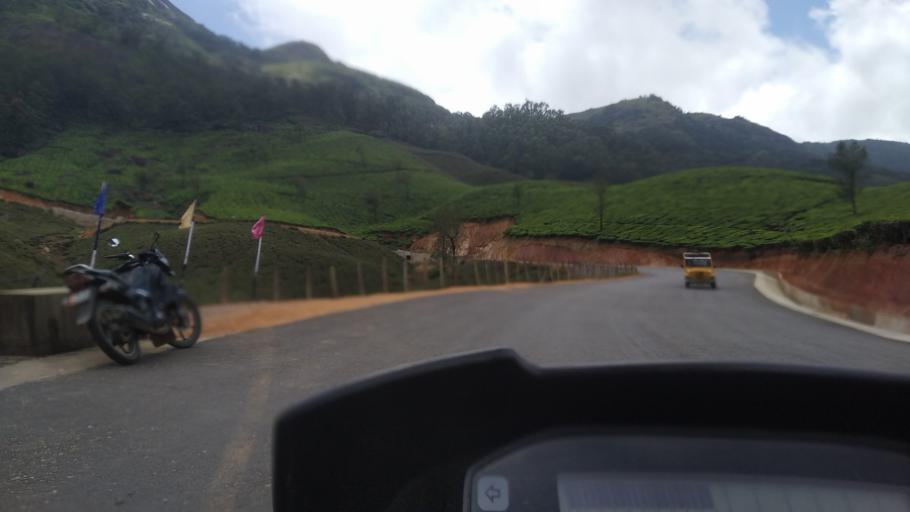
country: IN
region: Kerala
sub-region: Idukki
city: Munnar
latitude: 10.0454
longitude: 77.1125
